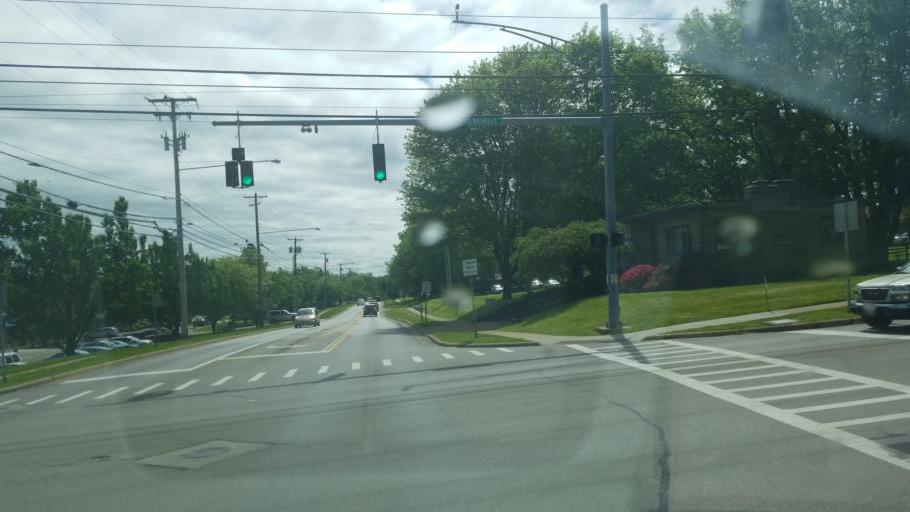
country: US
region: Ohio
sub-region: Wayne County
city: Wooster
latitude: 40.8432
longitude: -81.9399
